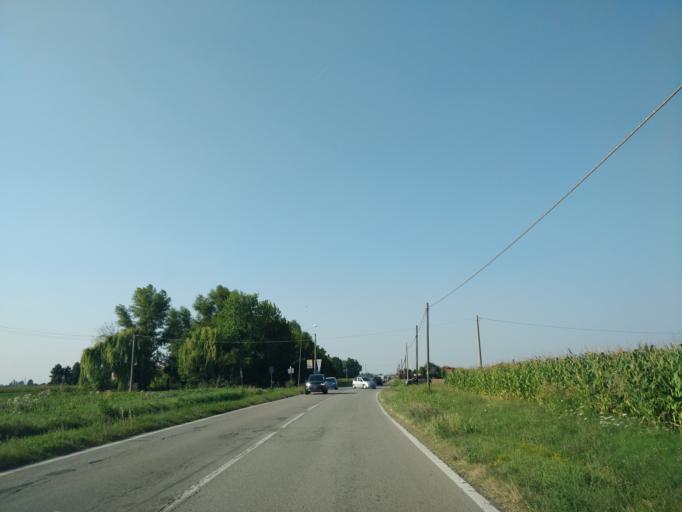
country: IT
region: Emilia-Romagna
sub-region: Provincia di Bologna
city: Argelato
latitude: 44.6124
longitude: 11.3356
